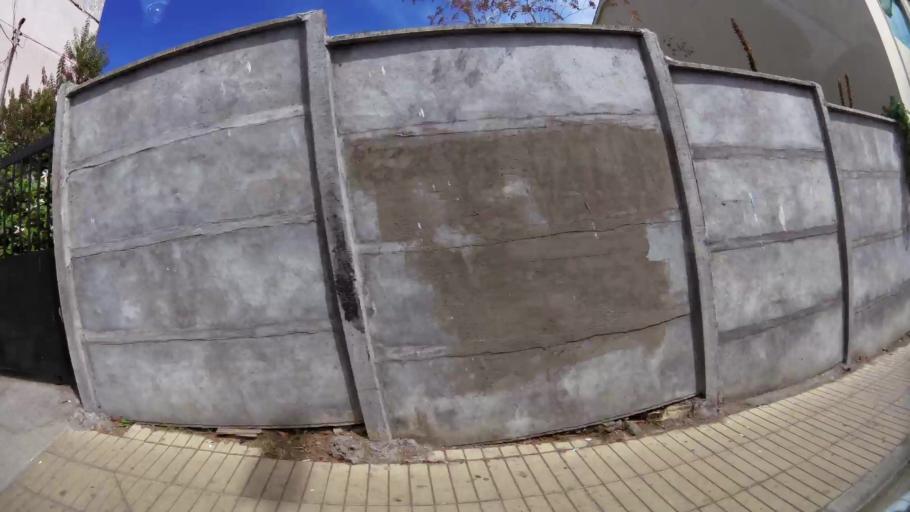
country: CL
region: Biobio
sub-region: Provincia de Concepcion
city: Talcahuano
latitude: -36.7156
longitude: -73.1141
